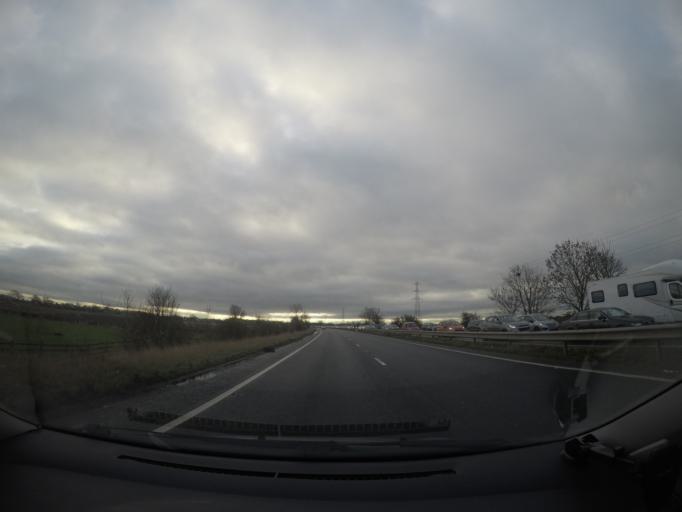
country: GB
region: England
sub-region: City of York
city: Murton
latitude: 53.9731
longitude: -1.0202
